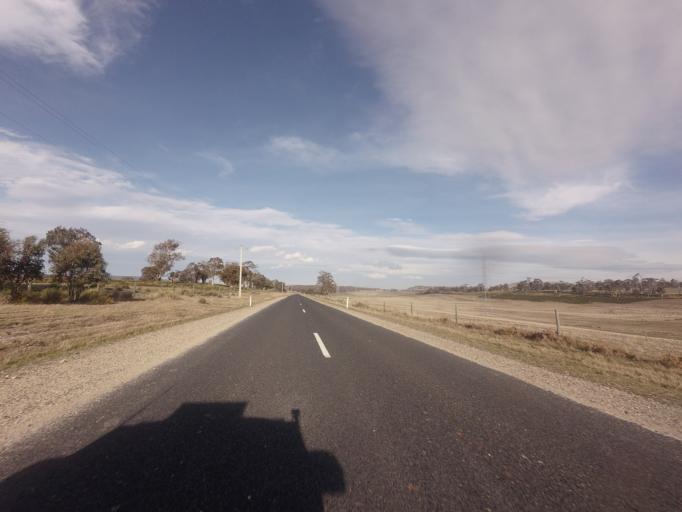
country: AU
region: Tasmania
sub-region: Derwent Valley
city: New Norfolk
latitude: -42.2527
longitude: 146.9310
